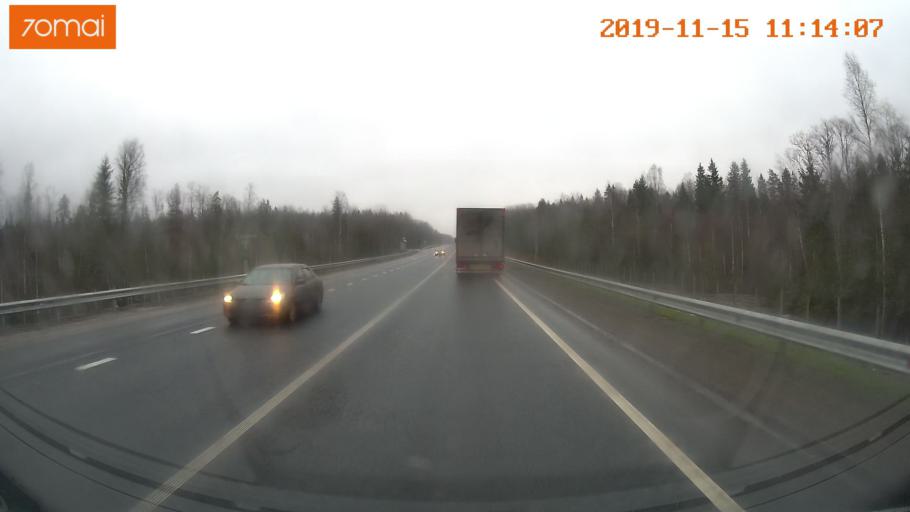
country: RU
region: Vologda
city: Chebsara
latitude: 59.1240
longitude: 39.1820
